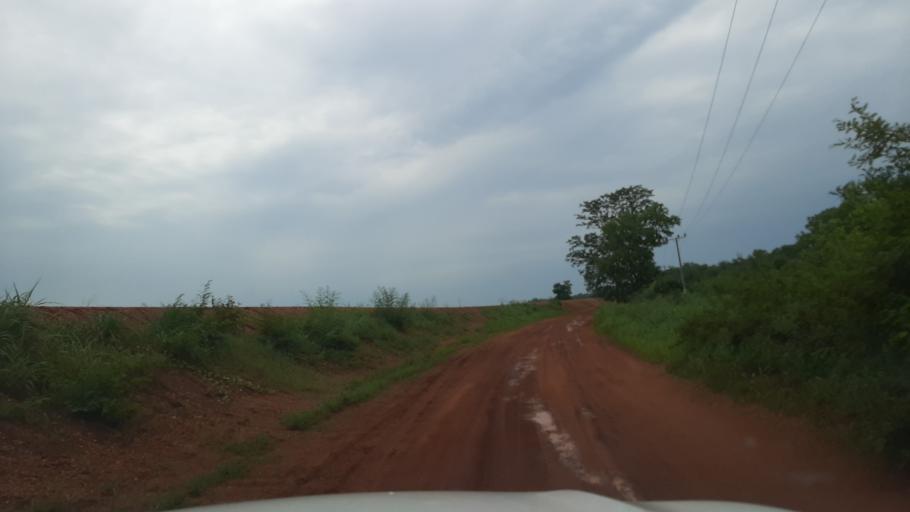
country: ET
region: Gambela
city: Gambela
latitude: 8.1460
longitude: 34.3605
